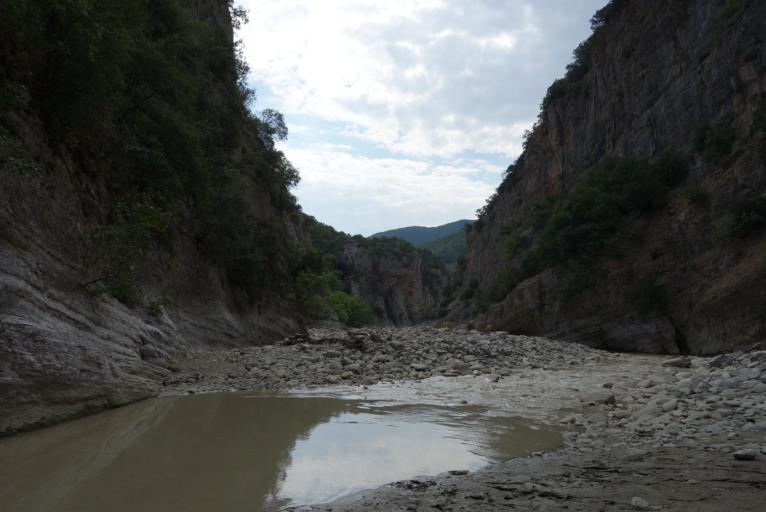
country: AL
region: Gjirokaster
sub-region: Rrethi i Permetit
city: Petran
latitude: 40.2450
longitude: 20.4375
